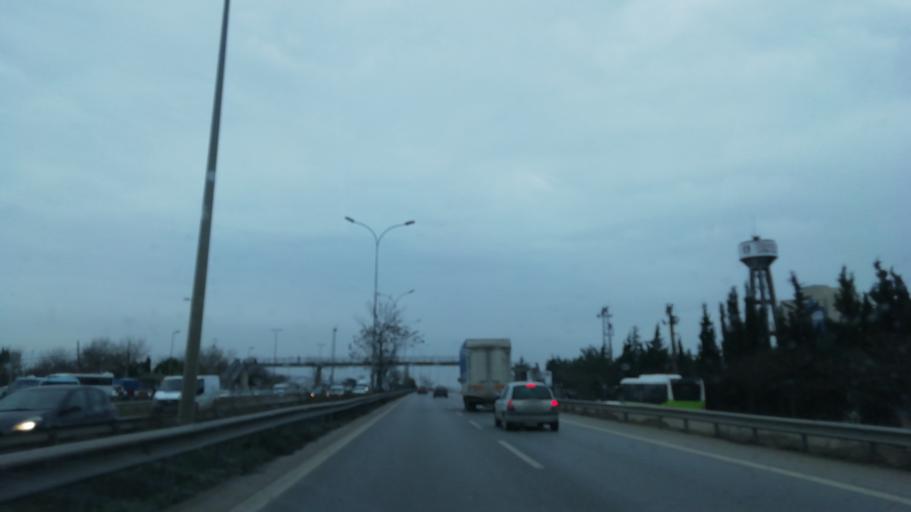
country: TR
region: Istanbul
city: Icmeler
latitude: 40.8234
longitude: 29.3522
